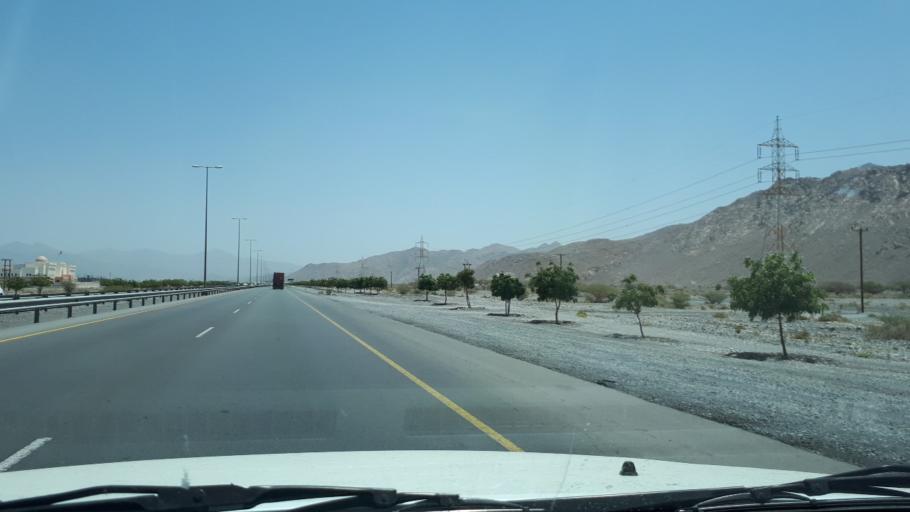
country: OM
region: Muhafazat ad Dakhiliyah
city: Nizwa
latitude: 22.8631
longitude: 57.5954
